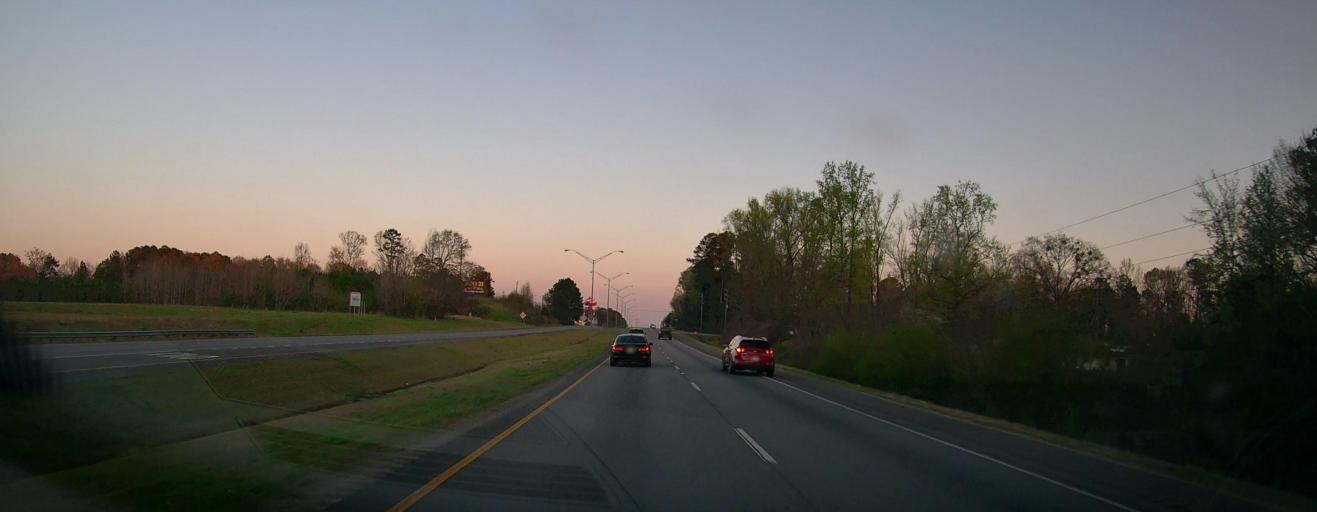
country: US
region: Alabama
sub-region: Tallapoosa County
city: Alexander City
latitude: 32.9382
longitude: -85.9770
